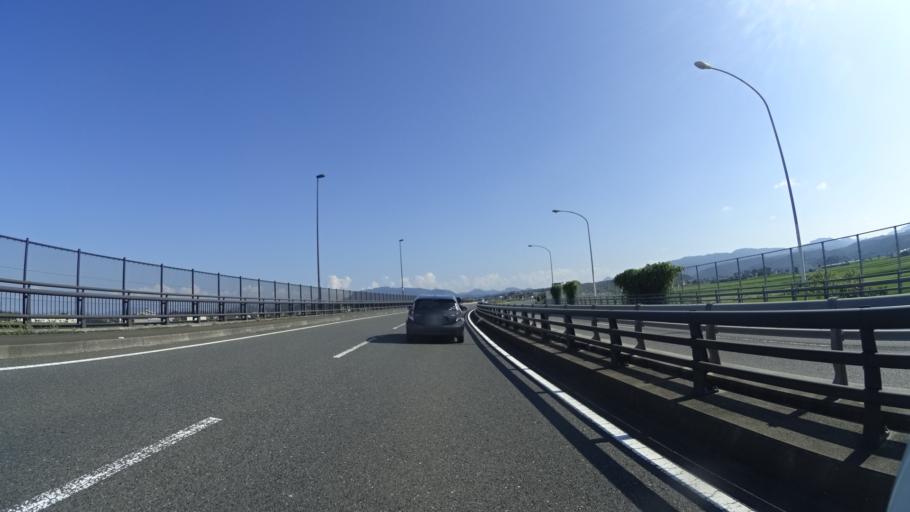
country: JP
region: Fukuoka
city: Yoshitomi
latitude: 33.5848
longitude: 131.1614
